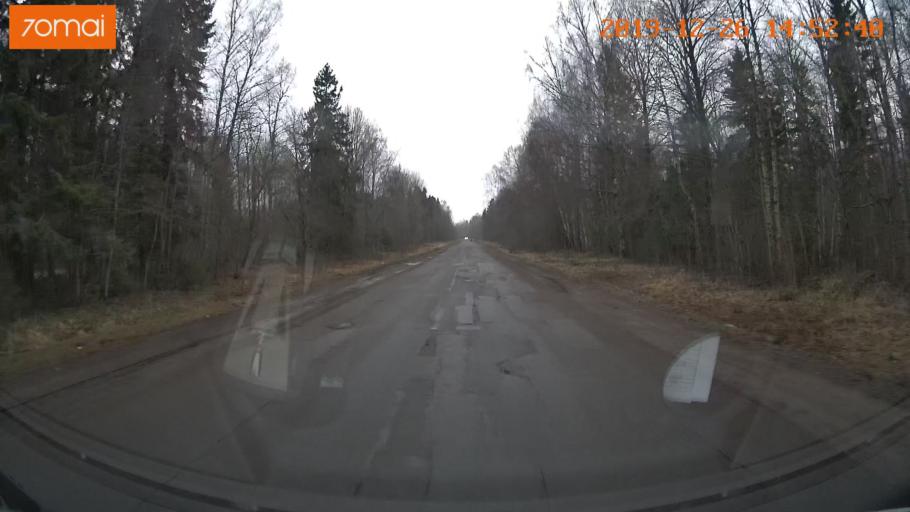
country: RU
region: Jaroslavl
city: Rybinsk
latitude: 58.3202
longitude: 38.8964
